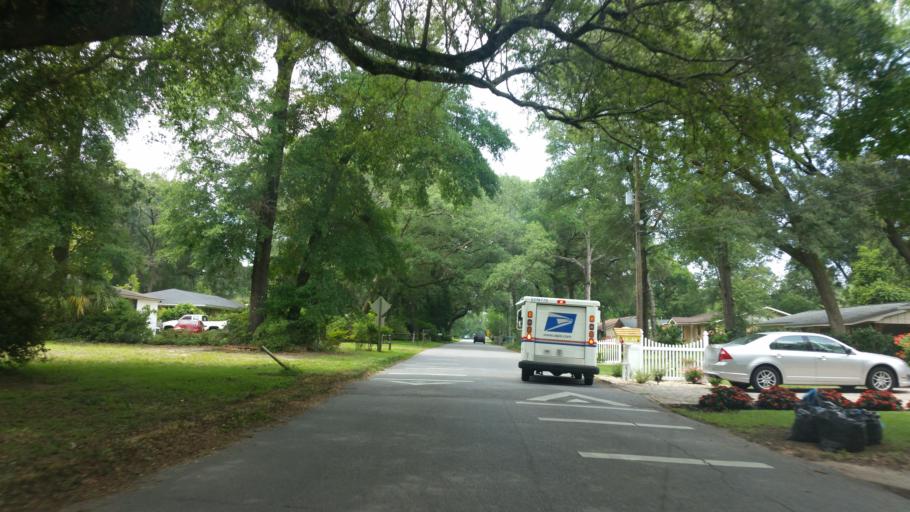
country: US
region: Florida
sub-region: Escambia County
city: Brent
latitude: 30.4855
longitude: -87.2405
